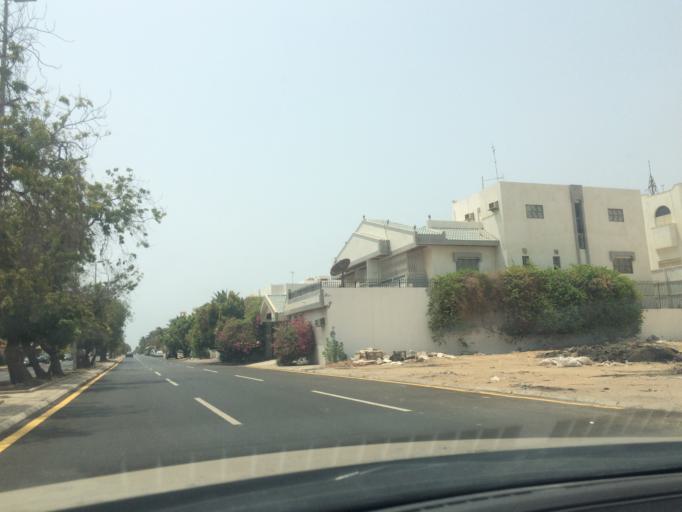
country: SA
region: Makkah
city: Jeddah
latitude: 21.5637
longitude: 39.1224
